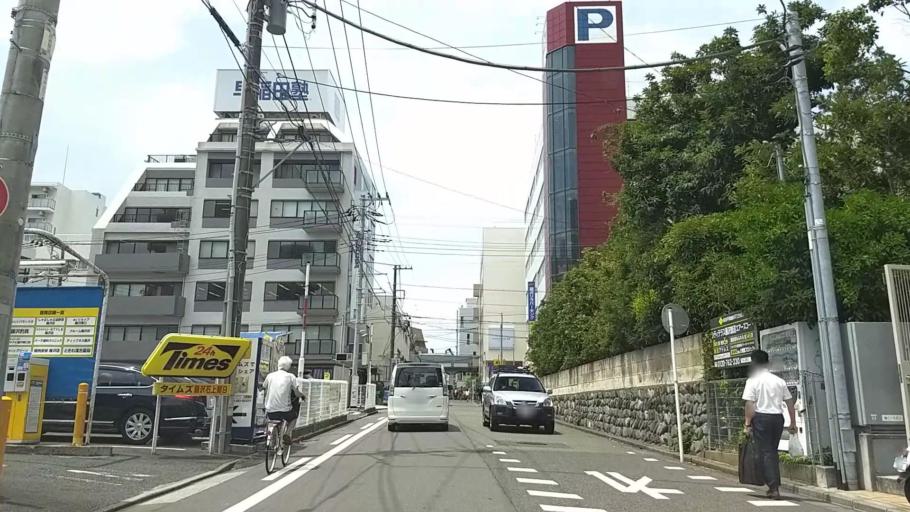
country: JP
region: Kanagawa
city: Fujisawa
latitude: 35.3358
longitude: 139.4877
